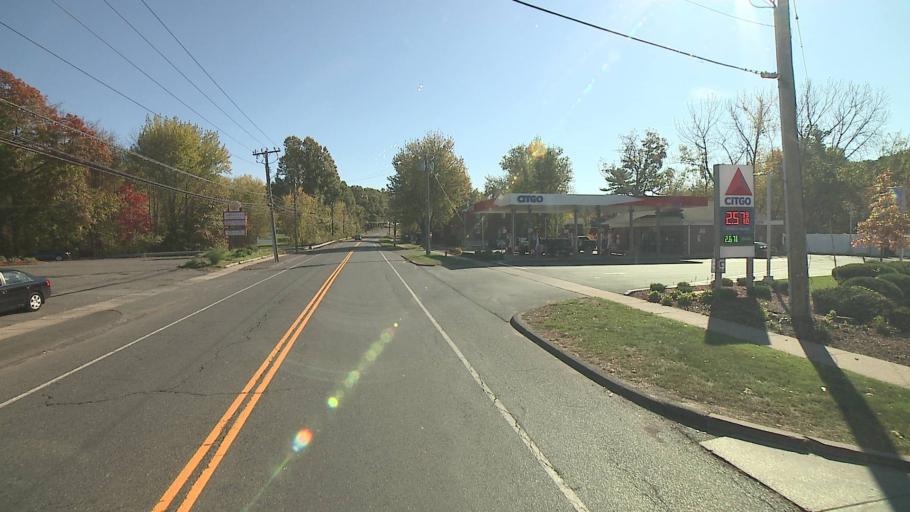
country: US
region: Connecticut
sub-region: Hartford County
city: East Hartford
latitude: 41.7836
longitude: -72.5843
